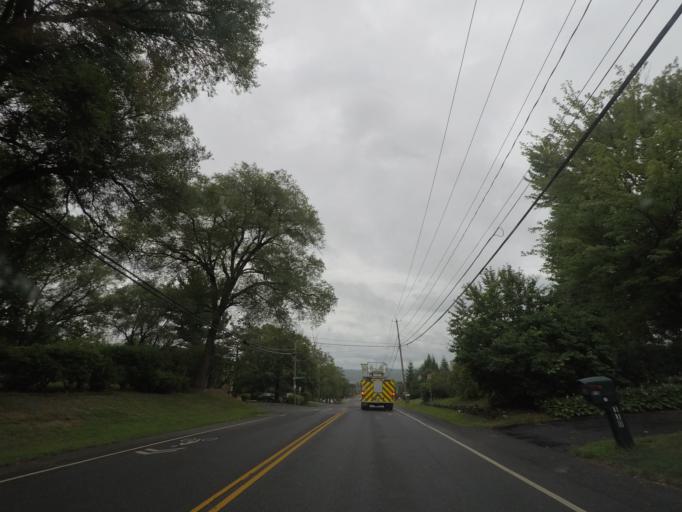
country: US
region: New York
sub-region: Albany County
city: Albany
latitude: 42.6748
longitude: -73.7531
